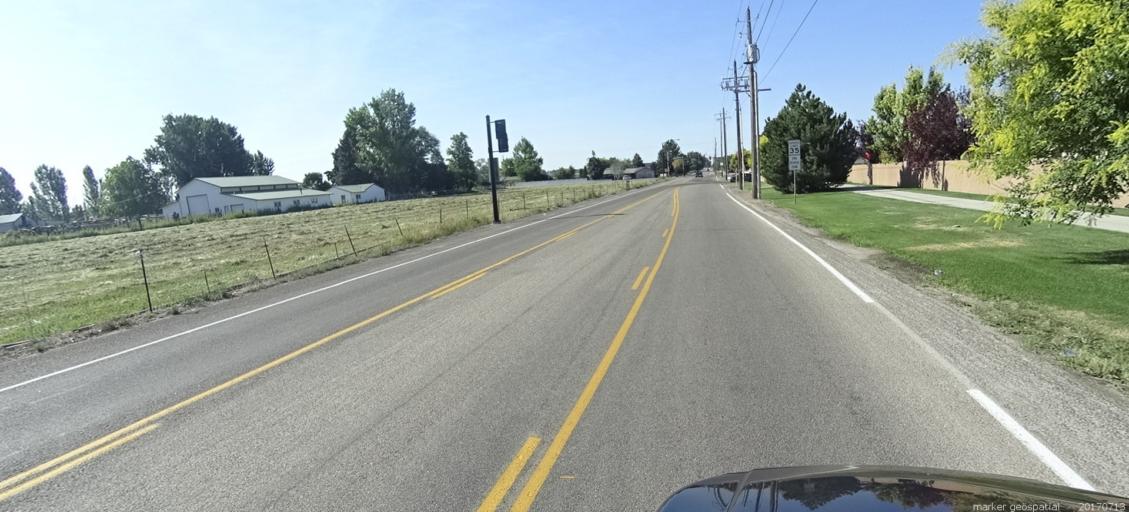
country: US
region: Idaho
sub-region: Ada County
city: Kuna
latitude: 43.5047
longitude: -116.4138
